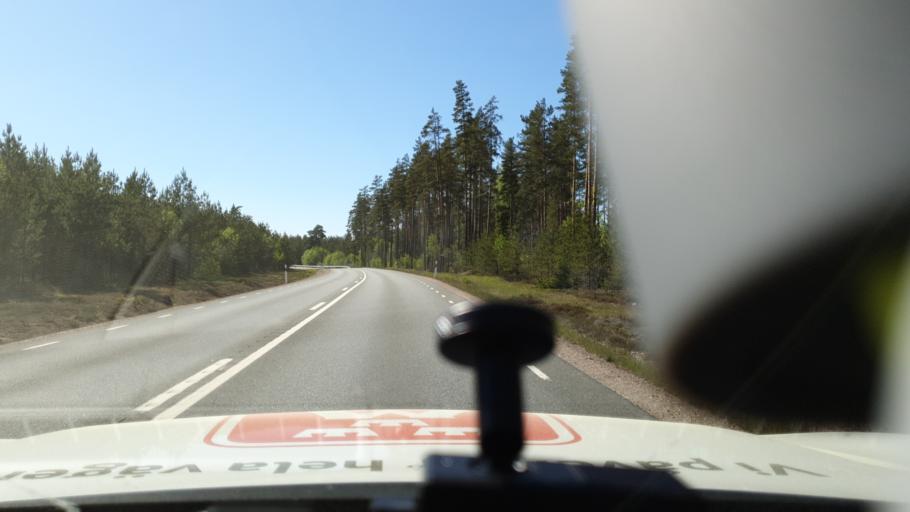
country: SE
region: Kalmar
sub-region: Hultsfreds Kommun
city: Virserum
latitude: 57.3985
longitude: 15.4251
